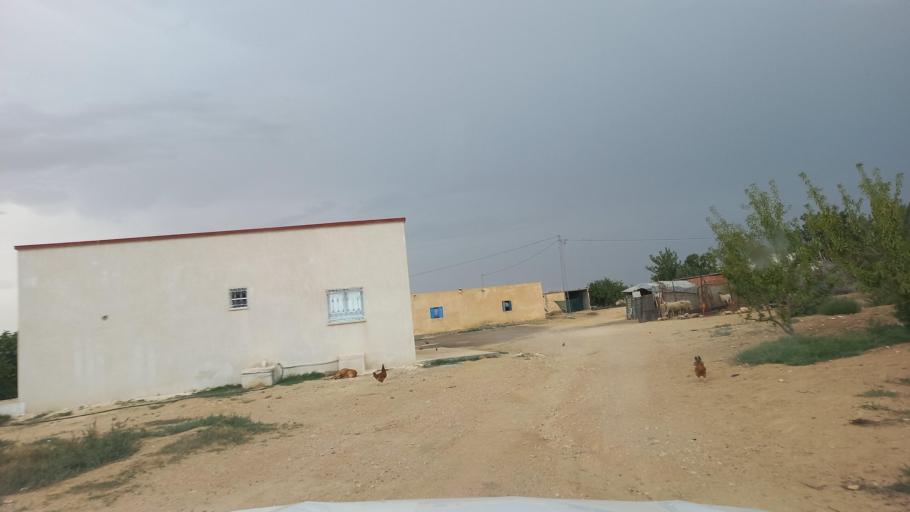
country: TN
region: Al Qasrayn
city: Kasserine
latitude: 35.2380
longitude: 9.0237
